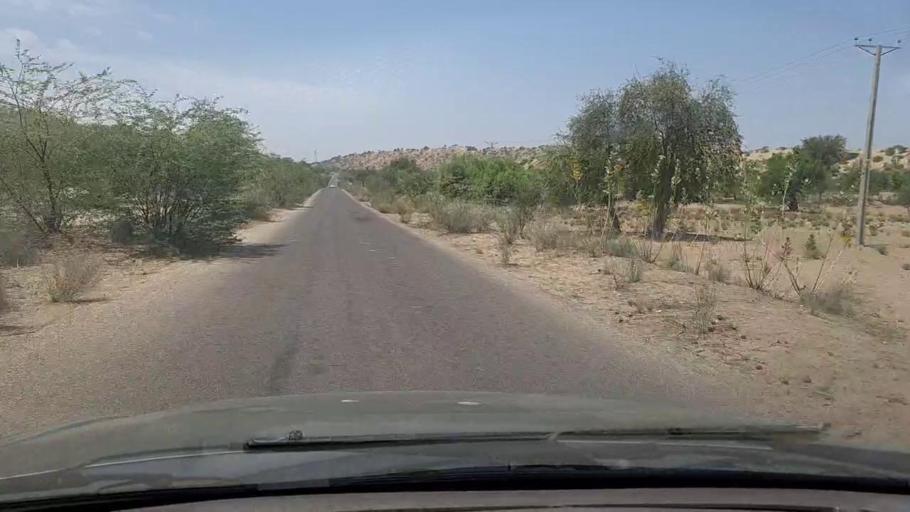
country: PK
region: Sindh
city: Diplo
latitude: 24.5592
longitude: 69.6678
